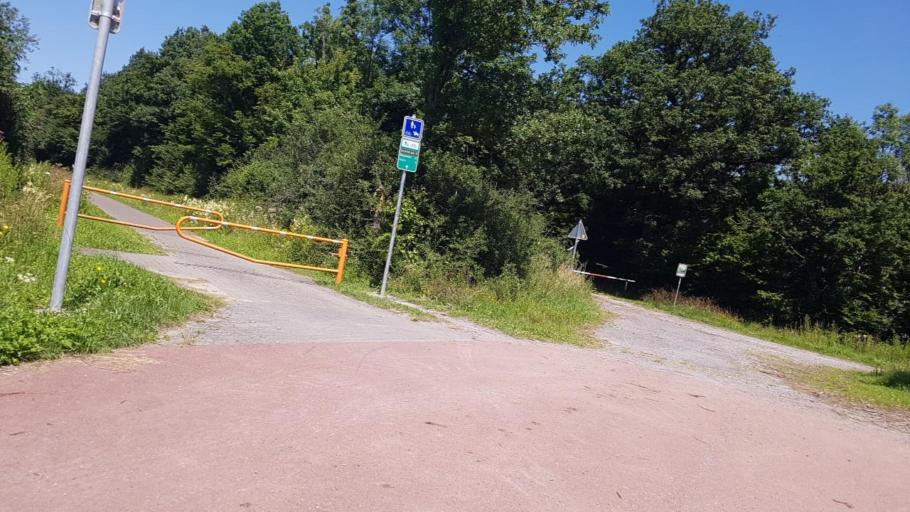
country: BE
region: Wallonia
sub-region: Province du Hainaut
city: Froidchapelle
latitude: 50.1514
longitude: 4.2733
